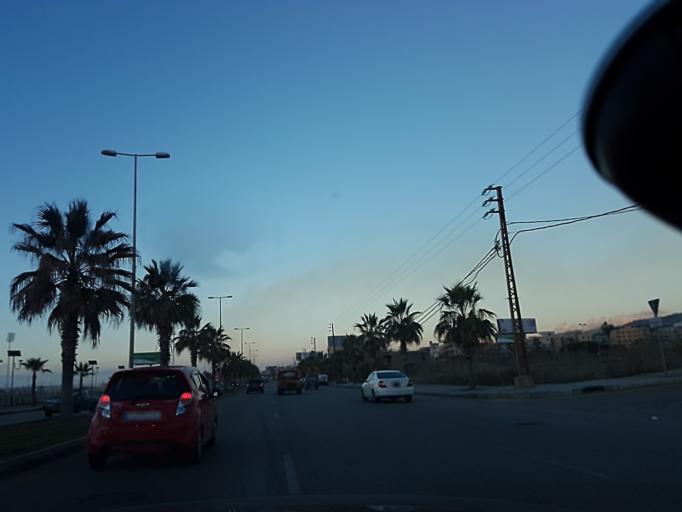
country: LB
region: Liban-Sud
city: Sidon
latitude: 33.5817
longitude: 35.3850
